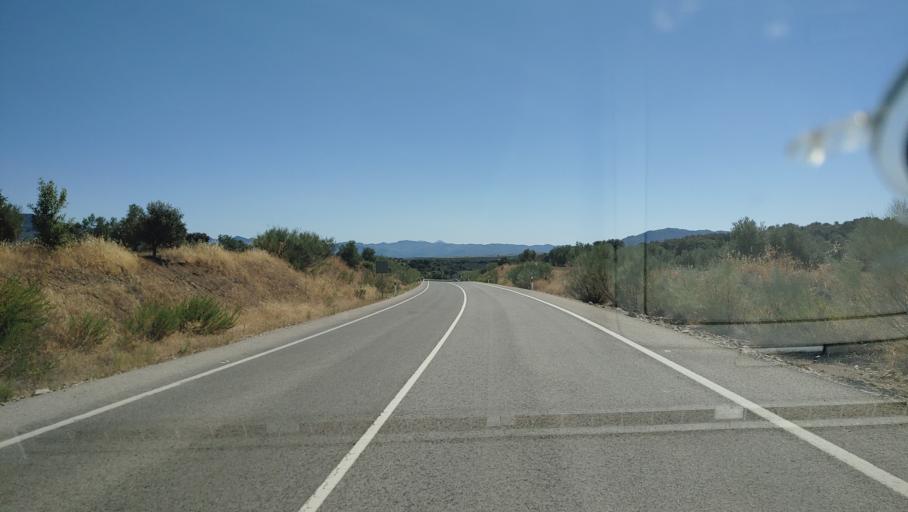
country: ES
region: Andalusia
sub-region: Provincia de Jaen
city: Genave
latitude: 38.4672
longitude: -2.7609
